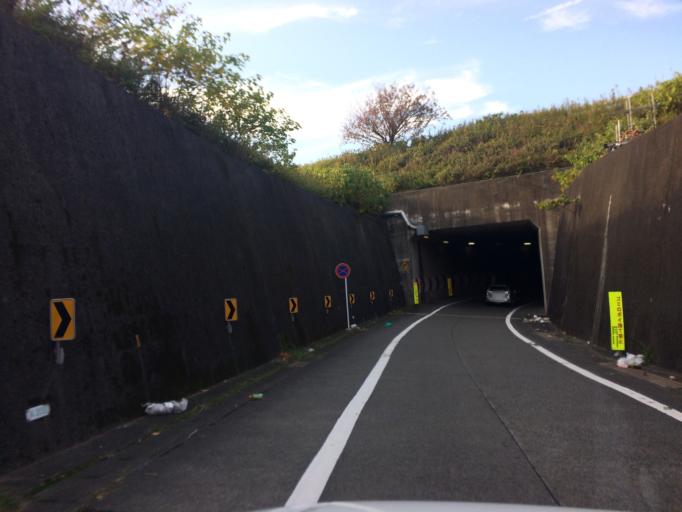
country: JP
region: Shizuoka
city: Fujieda
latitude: 34.8695
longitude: 138.2257
